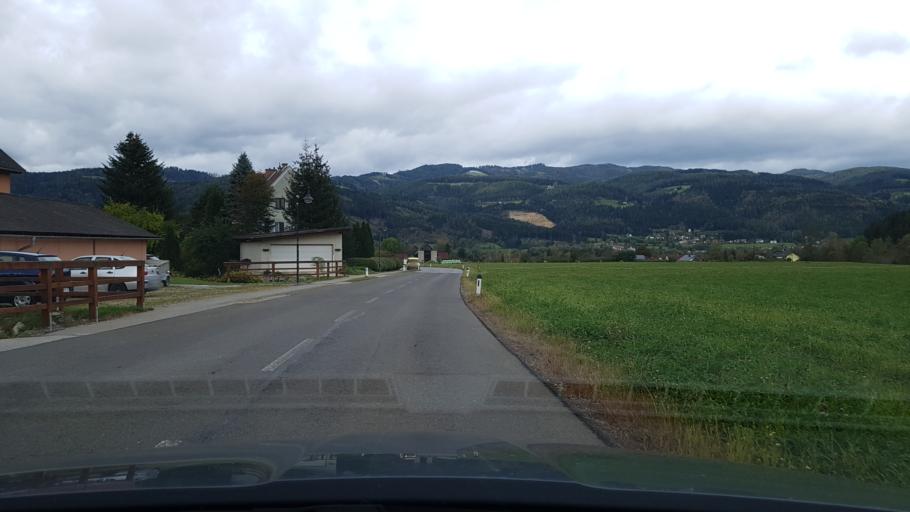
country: AT
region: Styria
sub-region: Politischer Bezirk Bruck-Muerzzuschlag
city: Allerheiligen im Muerztal
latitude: 47.4773
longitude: 15.4092
